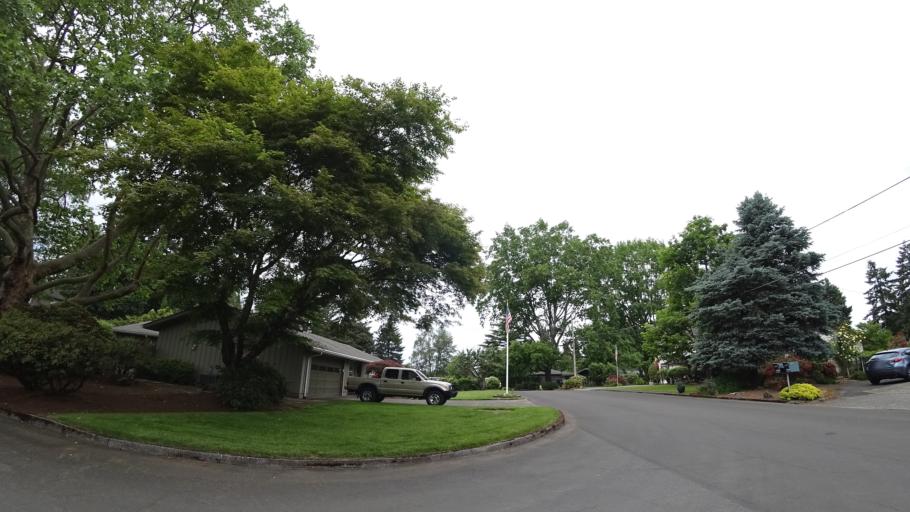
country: US
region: Oregon
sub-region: Washington County
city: Garden Home-Whitford
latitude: 45.4635
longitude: -122.7638
